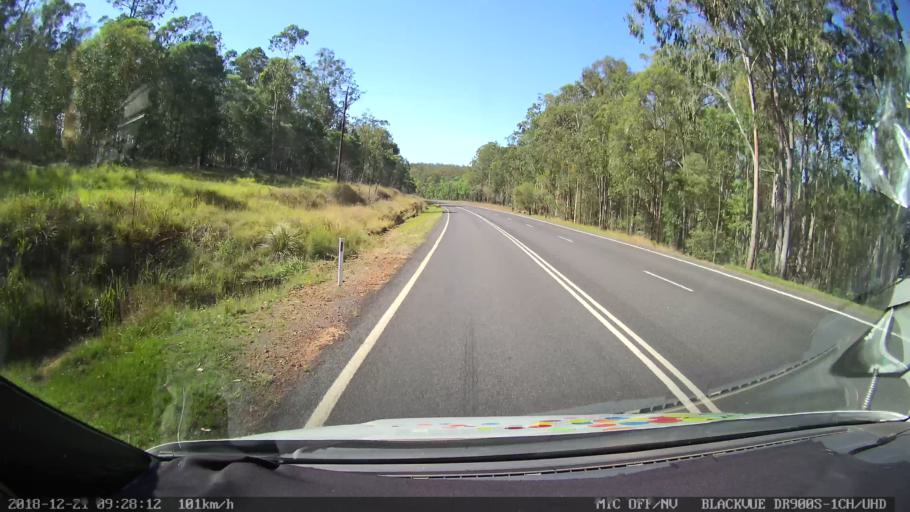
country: AU
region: New South Wales
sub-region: Clarence Valley
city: Maclean
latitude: -29.4139
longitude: 152.9864
